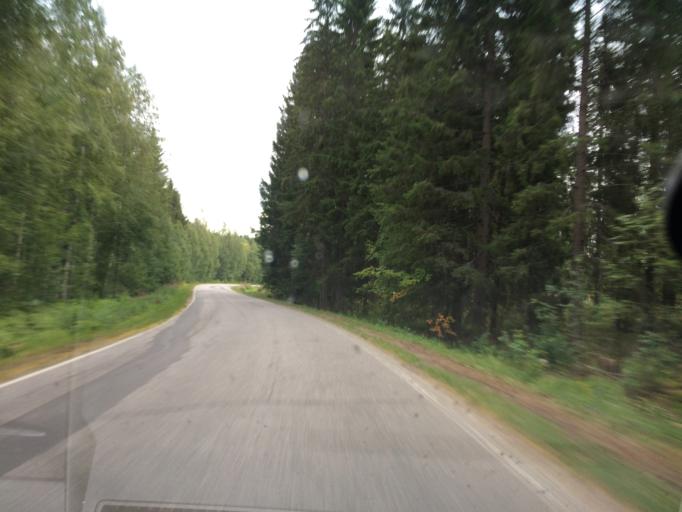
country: FI
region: Haeme
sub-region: Haemeenlinna
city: Tuulos
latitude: 61.1912
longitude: 24.7532
